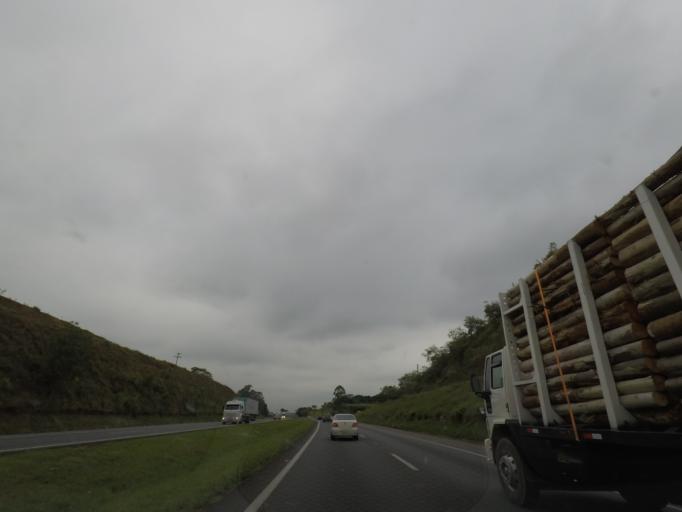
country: BR
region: Sao Paulo
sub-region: Itatiba
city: Itatiba
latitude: -23.0027
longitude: -46.7771
